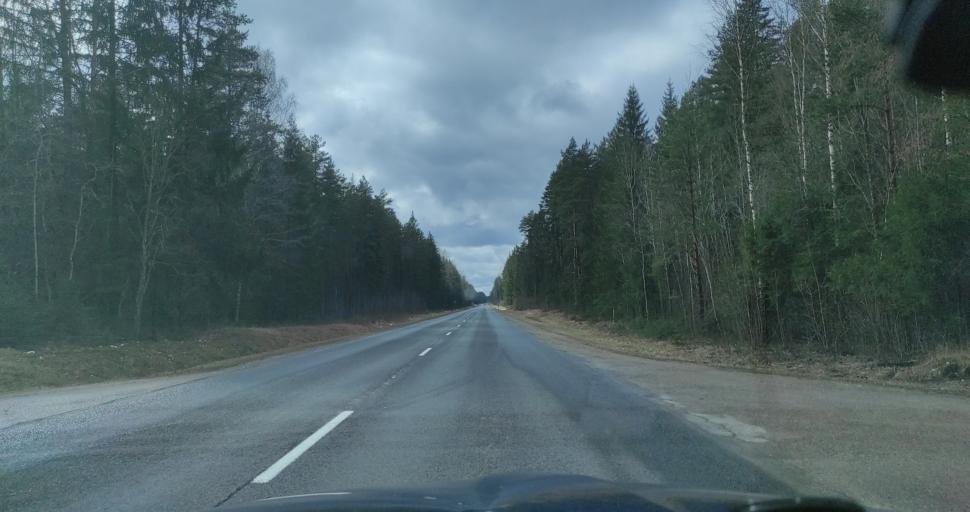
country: LV
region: Talsu Rajons
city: Stende
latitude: 57.1191
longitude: 22.5186
